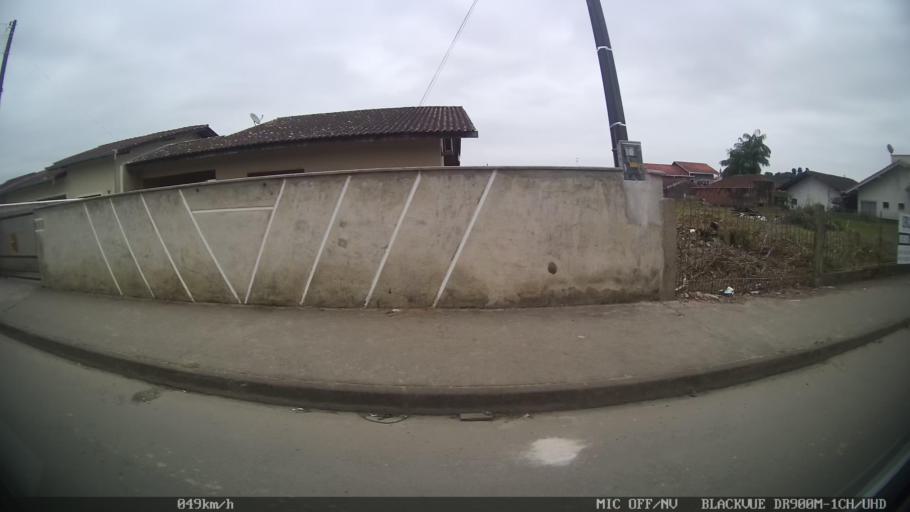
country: BR
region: Santa Catarina
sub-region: Joinville
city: Joinville
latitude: -26.3577
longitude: -48.8281
